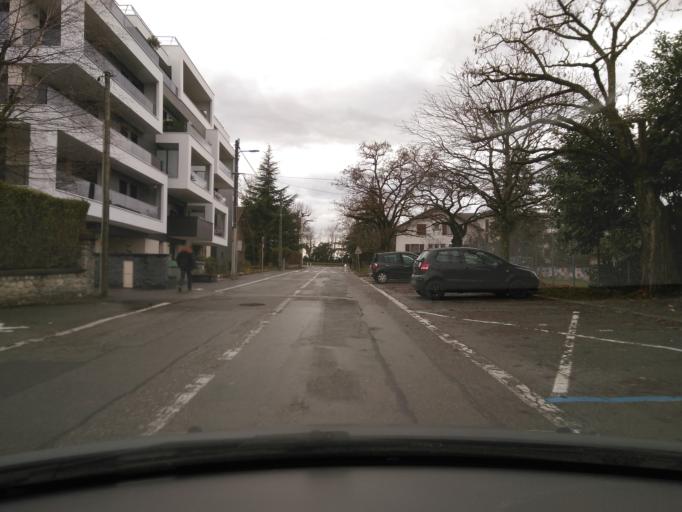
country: FR
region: Rhone-Alpes
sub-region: Departement de la Haute-Savoie
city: Saint-Julien-en-Genevois
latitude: 46.1447
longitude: 6.0865
